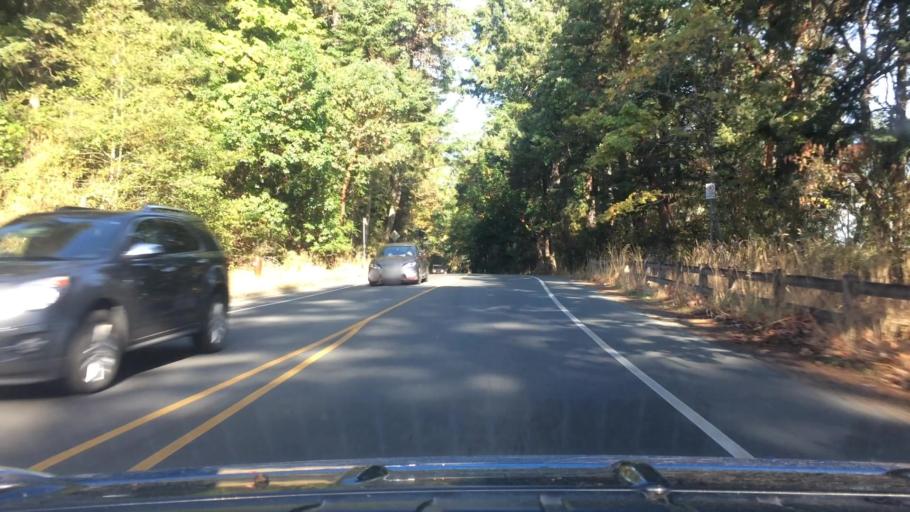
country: CA
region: British Columbia
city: Oak Bay
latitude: 48.4995
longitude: -123.3400
